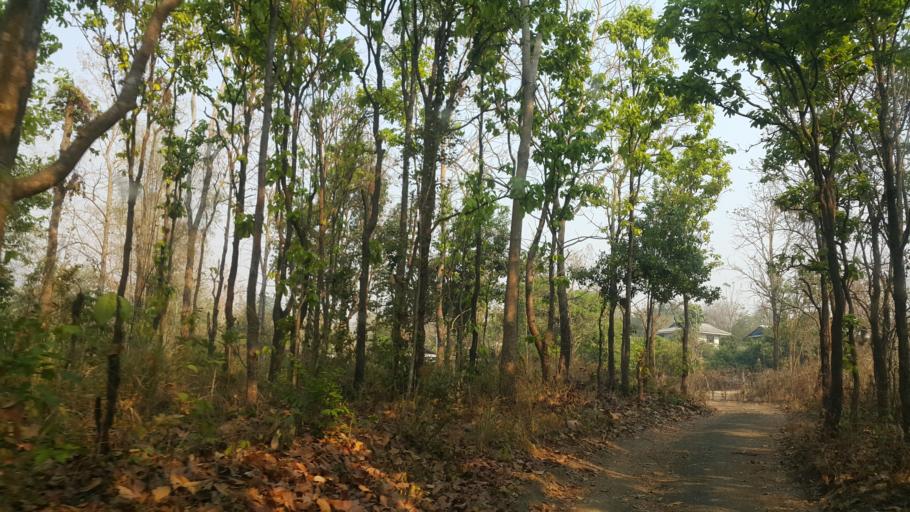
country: TH
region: Chiang Mai
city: Mae On
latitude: 18.7834
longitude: 99.2497
